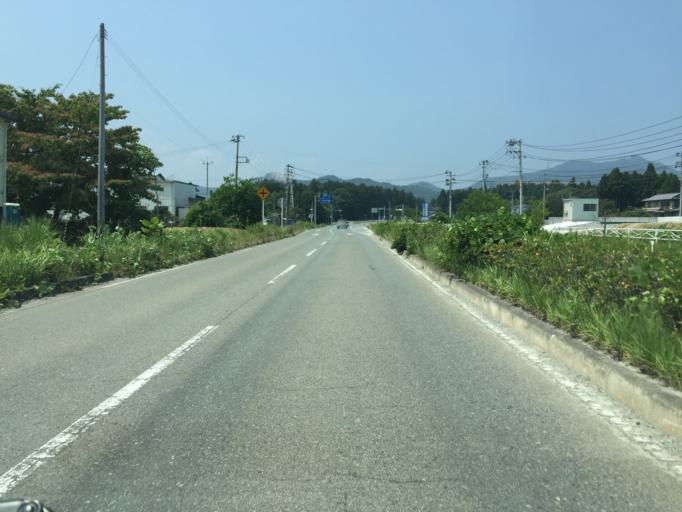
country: JP
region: Miyagi
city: Marumori
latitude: 37.8429
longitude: 140.8945
